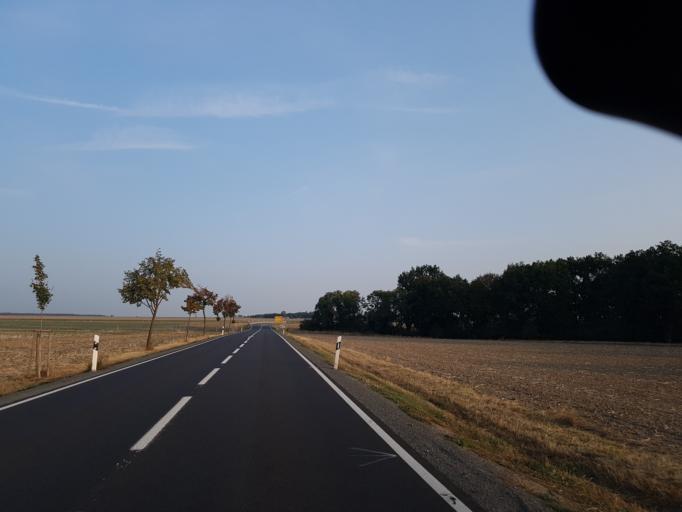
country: DE
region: Saxony
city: Zinna
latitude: 51.5861
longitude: 12.9543
